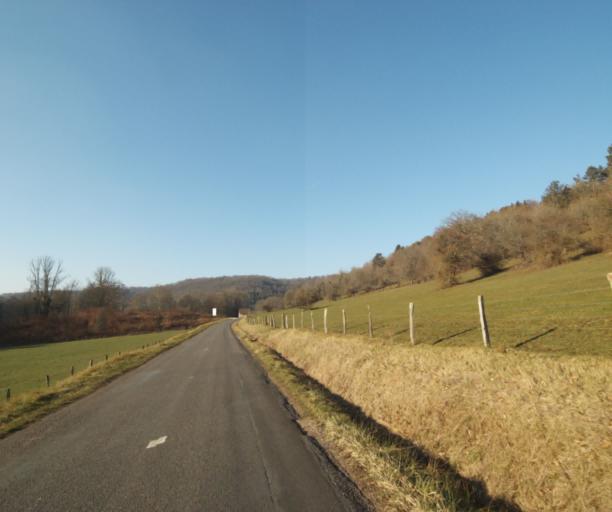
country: FR
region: Champagne-Ardenne
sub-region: Departement de la Haute-Marne
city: Chevillon
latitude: 48.5019
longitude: 5.1795
